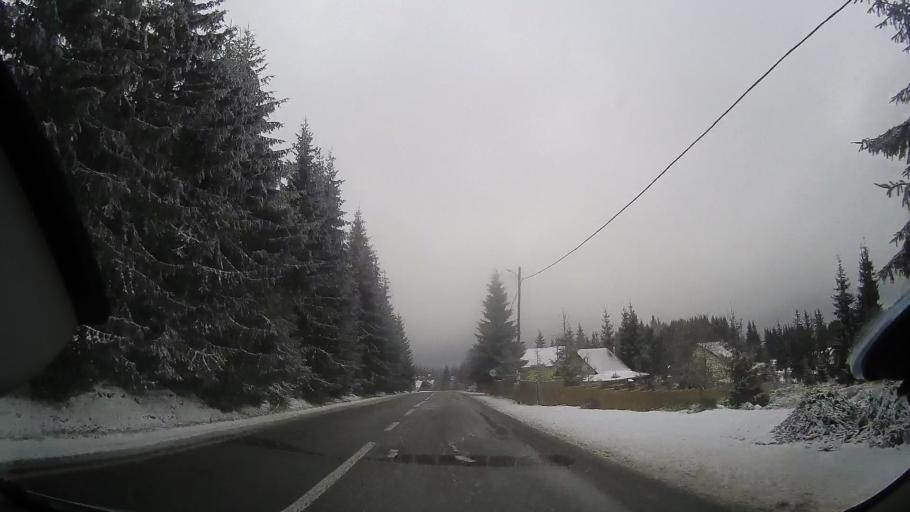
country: RO
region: Cluj
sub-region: Comuna Belis
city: Belis
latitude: 46.6803
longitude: 23.0392
